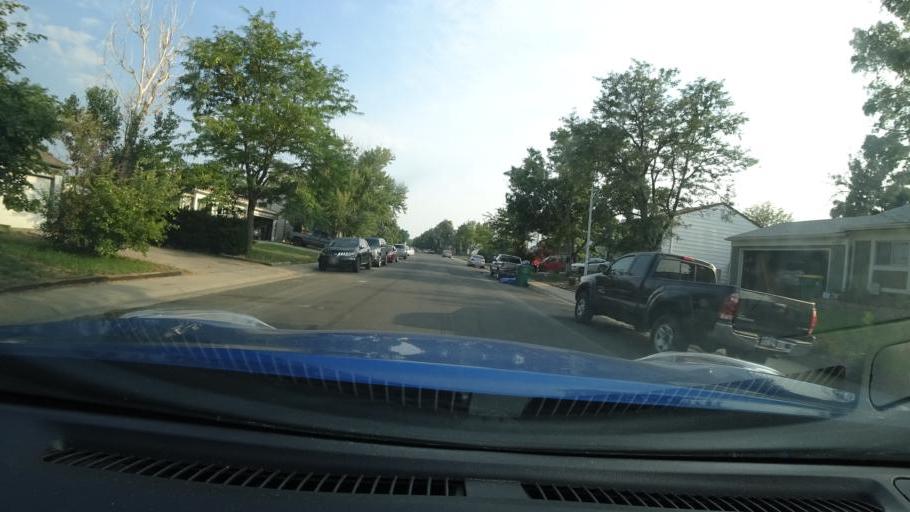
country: US
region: Colorado
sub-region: Adams County
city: Aurora
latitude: 39.7466
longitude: -104.7651
